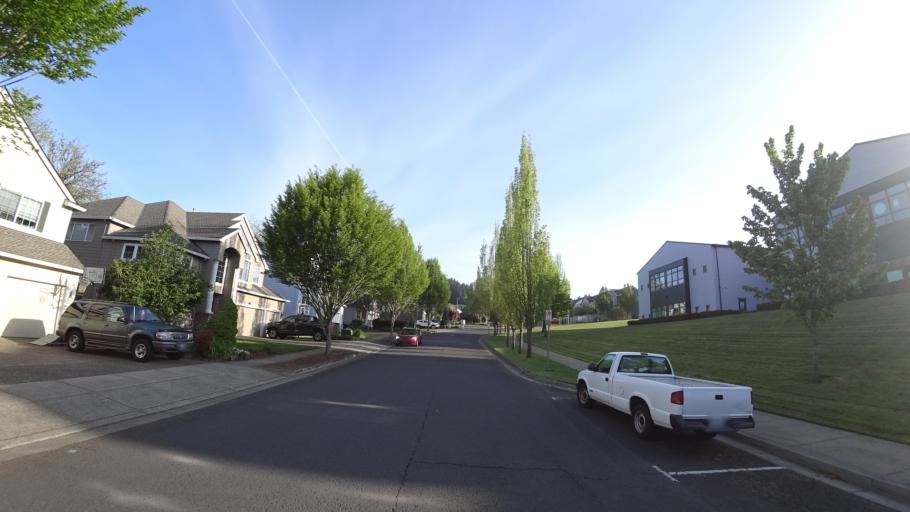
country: US
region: Oregon
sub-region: Washington County
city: King City
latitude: 45.4306
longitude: -122.8461
